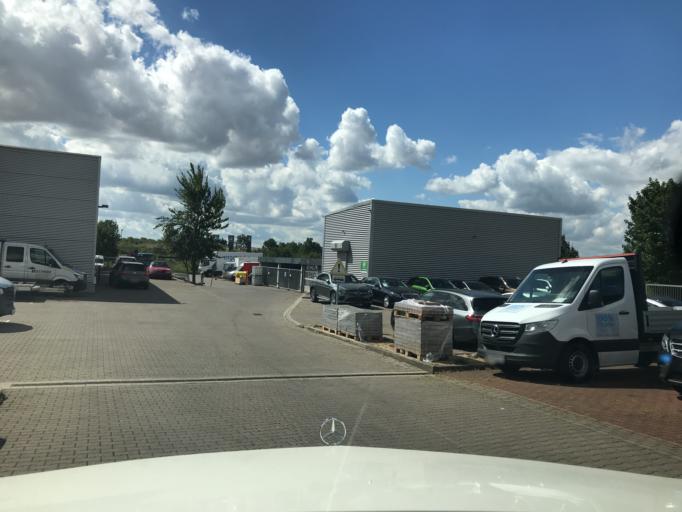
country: DE
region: Thuringia
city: Muehlhausen
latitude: 51.1947
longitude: 10.4858
